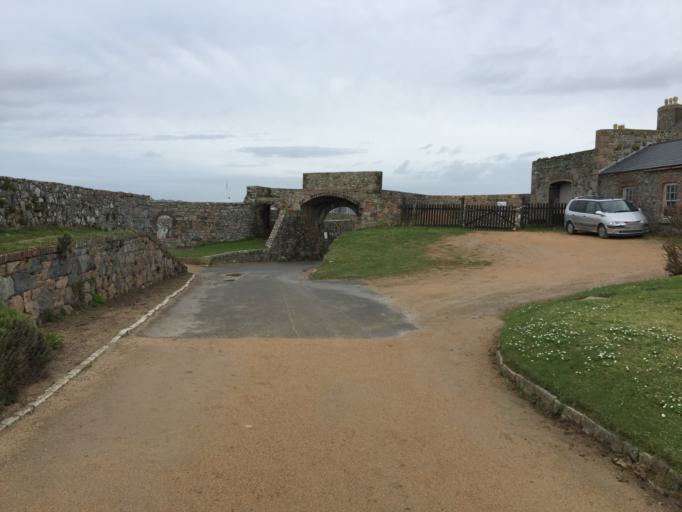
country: JE
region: St Helier
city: Saint Helier
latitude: 49.1777
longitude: -2.1248
